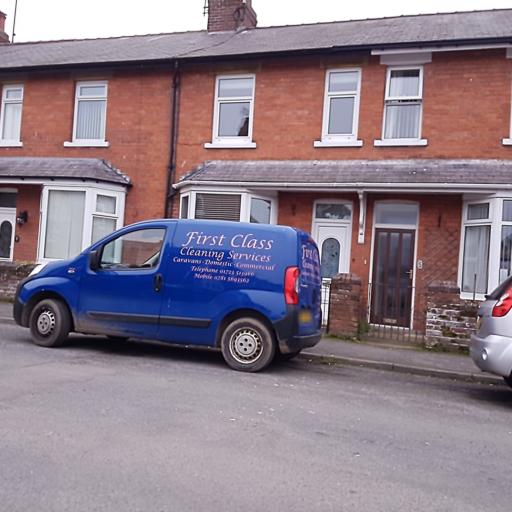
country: GB
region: England
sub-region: North Yorkshire
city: Filey
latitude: 54.2106
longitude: -0.2903
